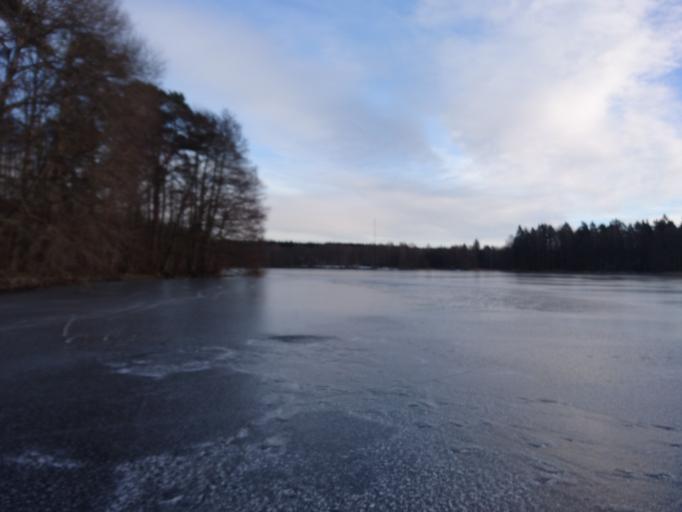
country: SE
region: Blekinge
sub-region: Karlshamns Kommun
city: Karlshamn
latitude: 56.2365
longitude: 14.9695
